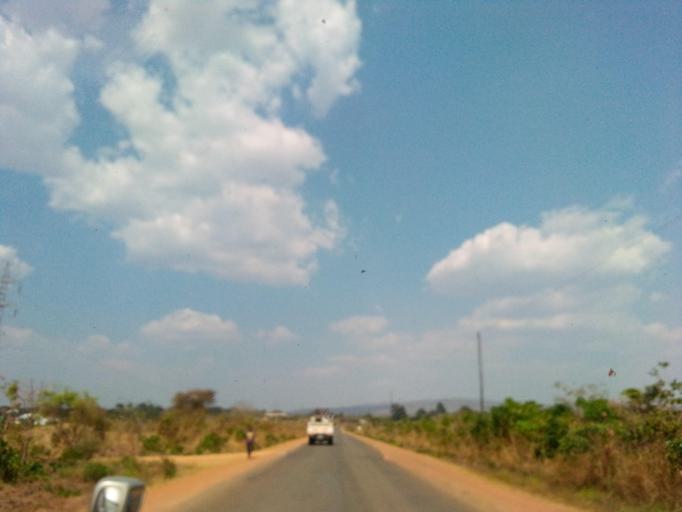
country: ZM
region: Northern
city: Mpika
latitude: -11.8331
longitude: 31.4153
